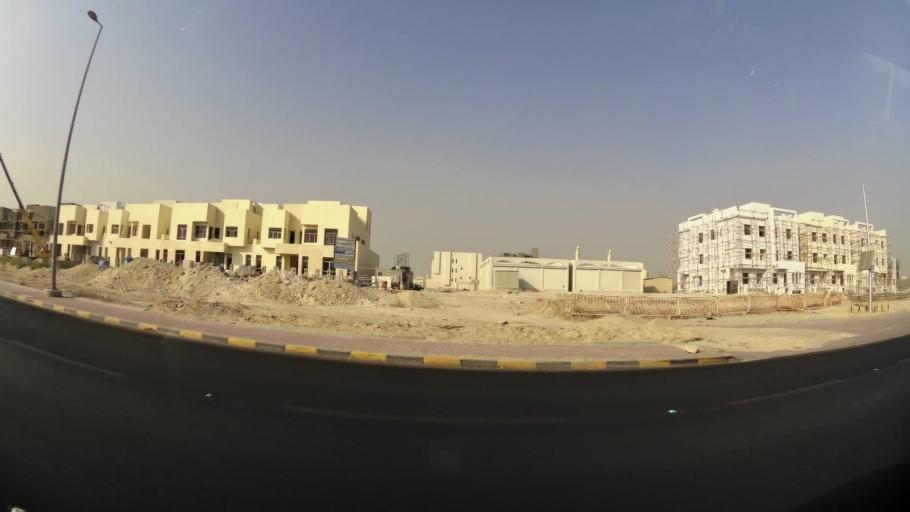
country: KW
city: Al Funaytis
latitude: 29.2244
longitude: 48.0995
